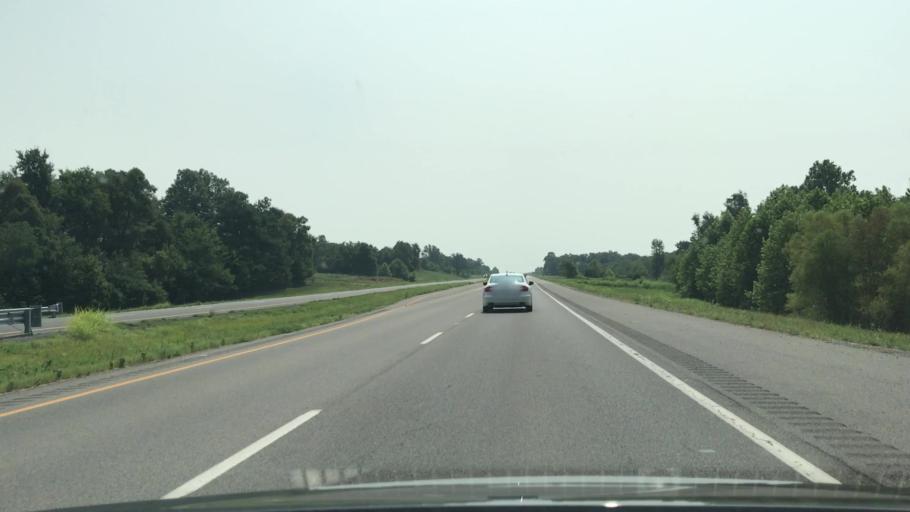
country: US
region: Kentucky
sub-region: Graves County
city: Mayfield
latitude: 36.6683
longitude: -88.4950
